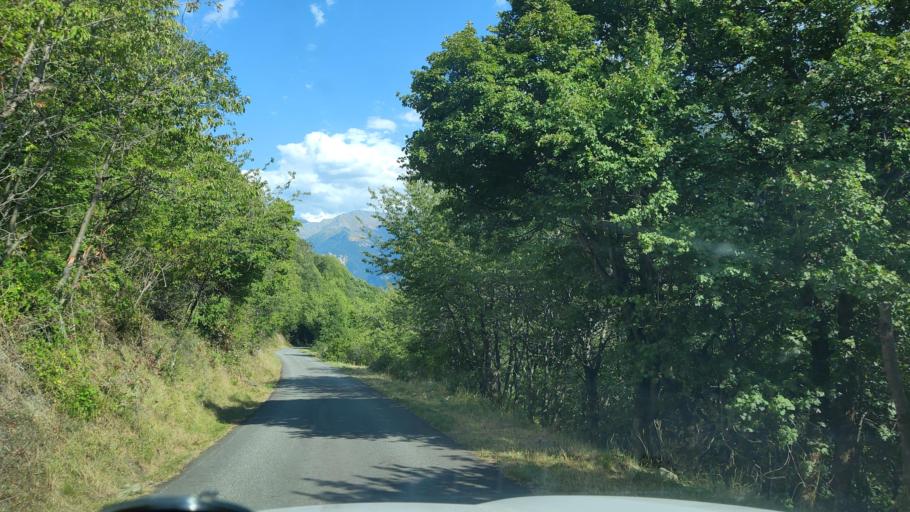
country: FR
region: Rhone-Alpes
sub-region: Departement de la Savoie
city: Val Thorens
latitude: 45.2136
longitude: 6.5625
